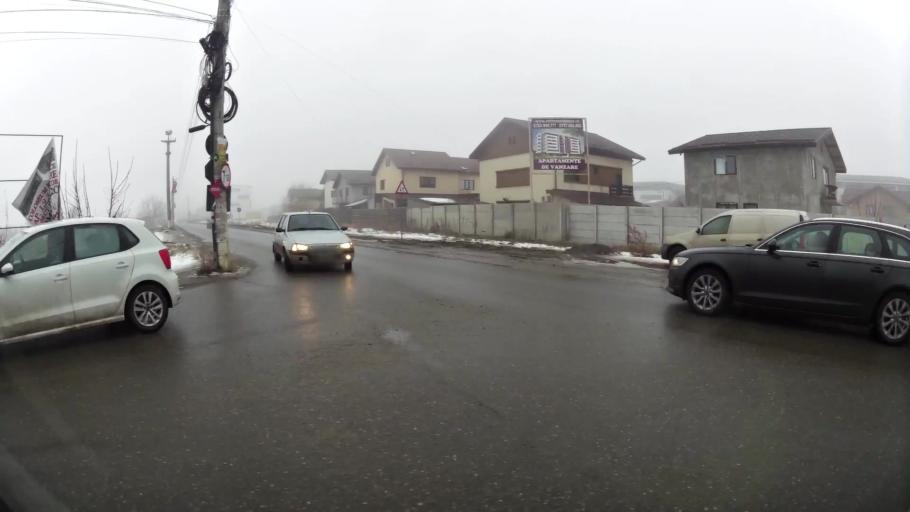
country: RO
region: Ilfov
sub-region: Comuna Chiajna
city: Chiajna
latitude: 44.4501
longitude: 25.9812
